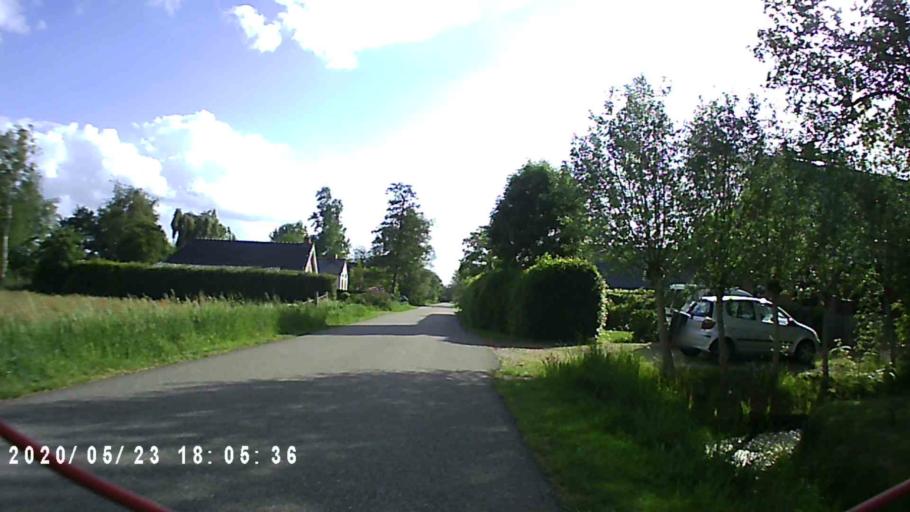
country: NL
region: Groningen
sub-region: Gemeente Slochteren
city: Slochteren
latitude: 53.2409
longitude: 6.7184
